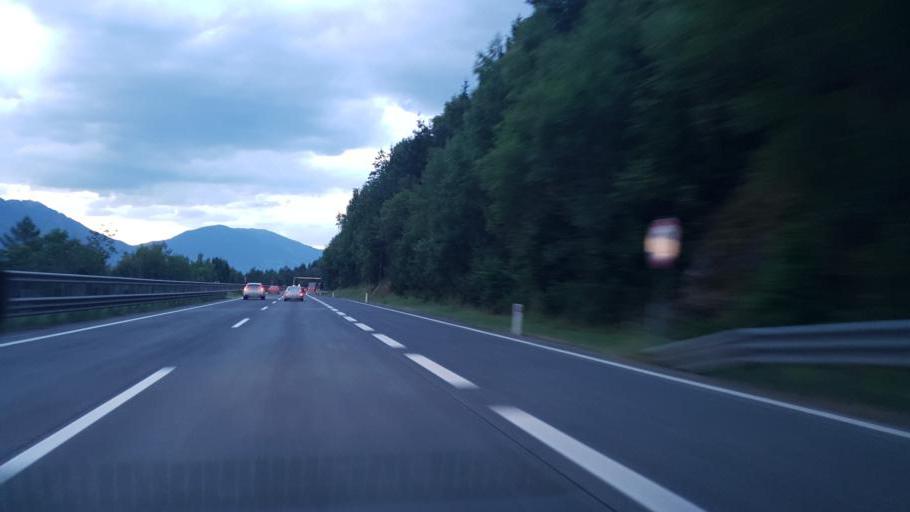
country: AT
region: Carinthia
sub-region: Politischer Bezirk Spittal an der Drau
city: Seeboden
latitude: 46.8099
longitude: 13.5122
